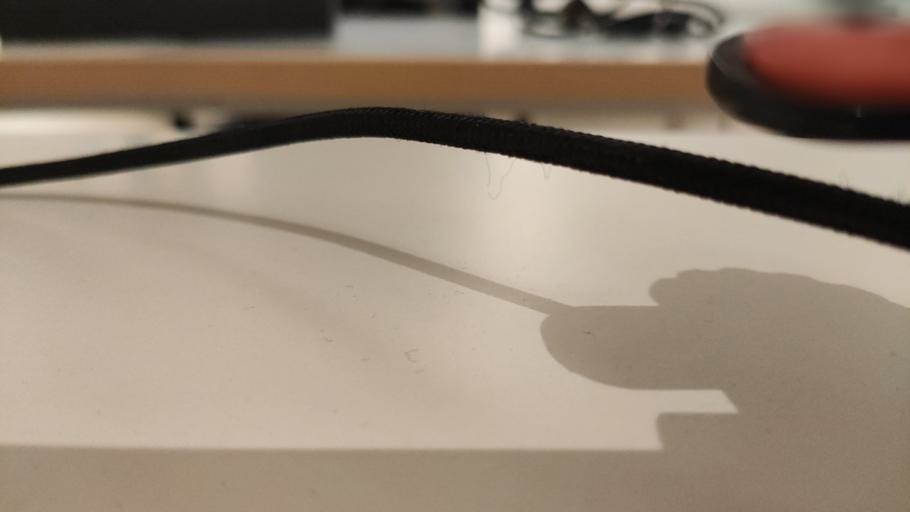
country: RU
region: Moskovskaya
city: Dorokhovo
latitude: 55.3942
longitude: 36.3880
